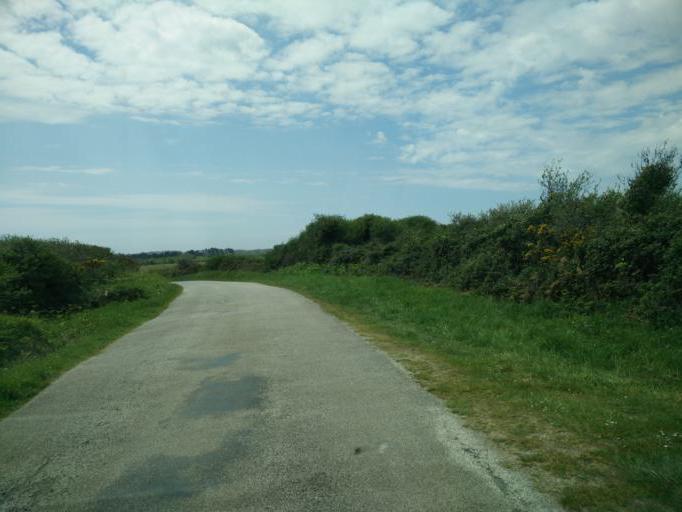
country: FR
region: Brittany
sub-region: Departement du Finistere
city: Roscanvel
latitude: 48.3388
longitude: -4.5406
